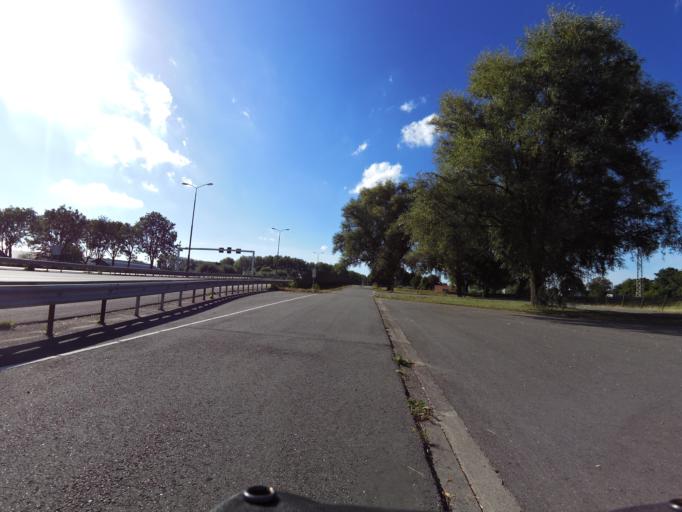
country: NL
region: South Holland
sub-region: Gemeente Zwijndrecht
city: Zwijndrecht
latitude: 51.7729
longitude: 4.6188
